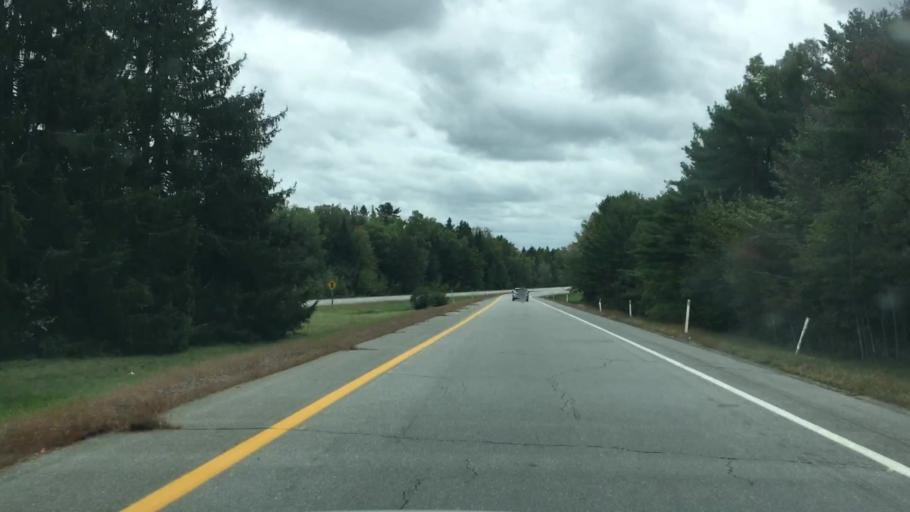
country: US
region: Maine
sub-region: Penobscot County
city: Milford
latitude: 44.9594
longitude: -68.7087
